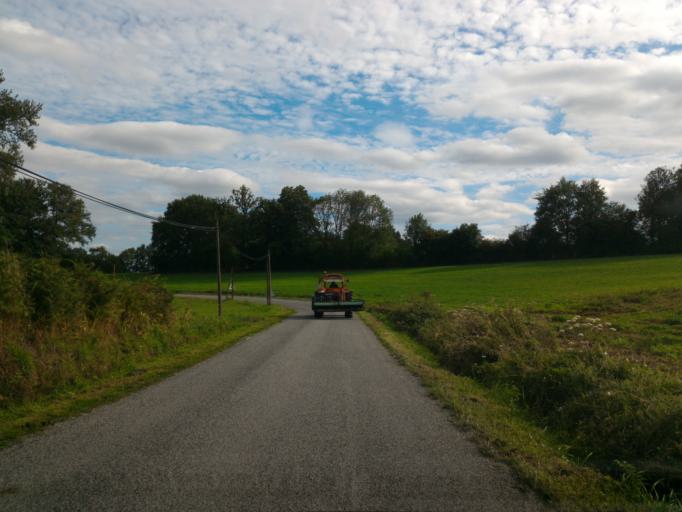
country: FR
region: Poitou-Charentes
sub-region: Departement de la Charente
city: Brigueuil
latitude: 45.9098
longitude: 0.8585
